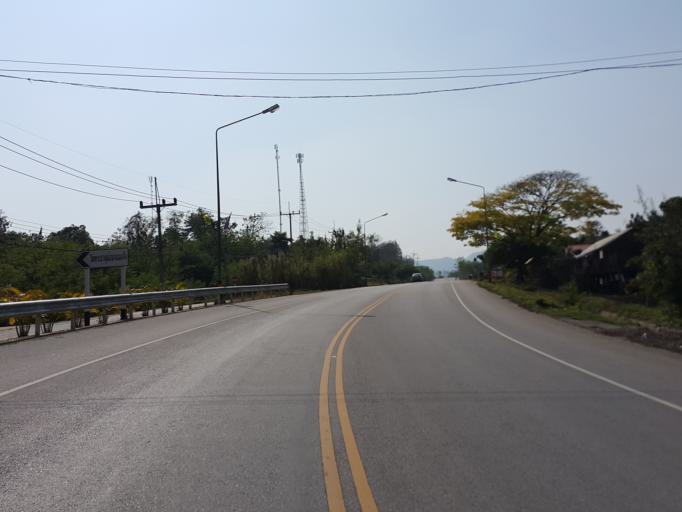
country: TH
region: Lampang
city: Wang Nuea
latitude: 18.9869
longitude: 99.6159
